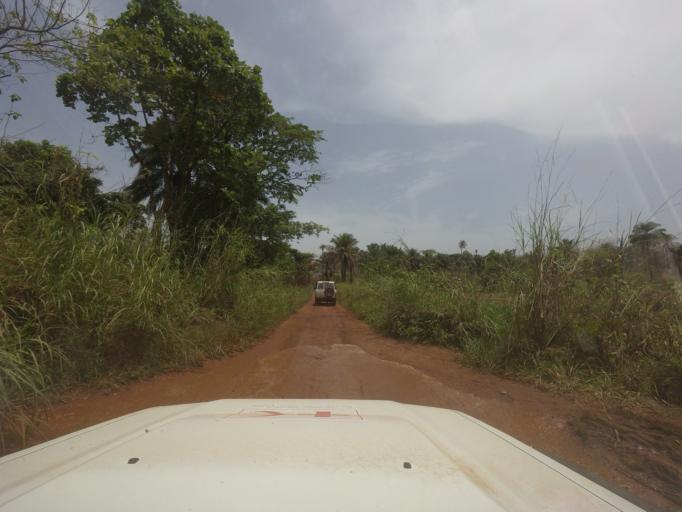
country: SL
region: Eastern Province
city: Buedu
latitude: 8.4696
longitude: -10.3332
